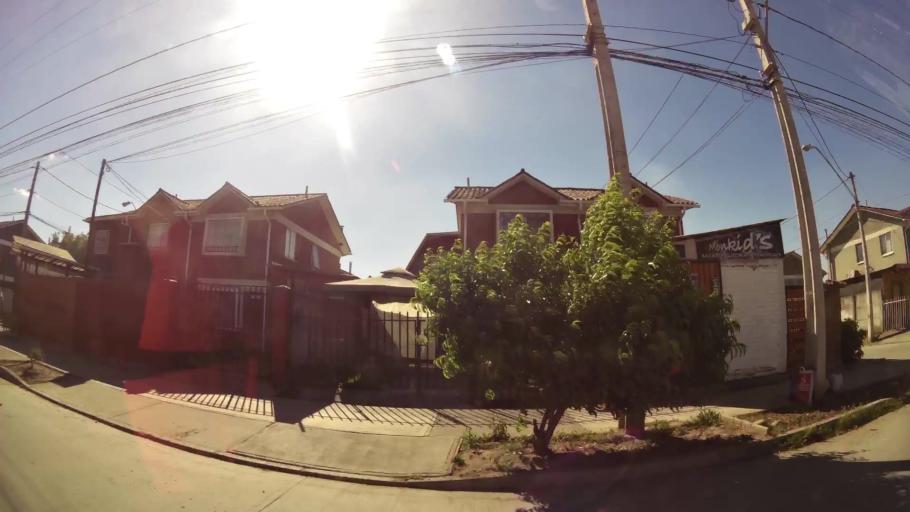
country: CL
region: Santiago Metropolitan
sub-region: Provincia de Maipo
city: San Bernardo
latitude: -33.5510
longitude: -70.7670
